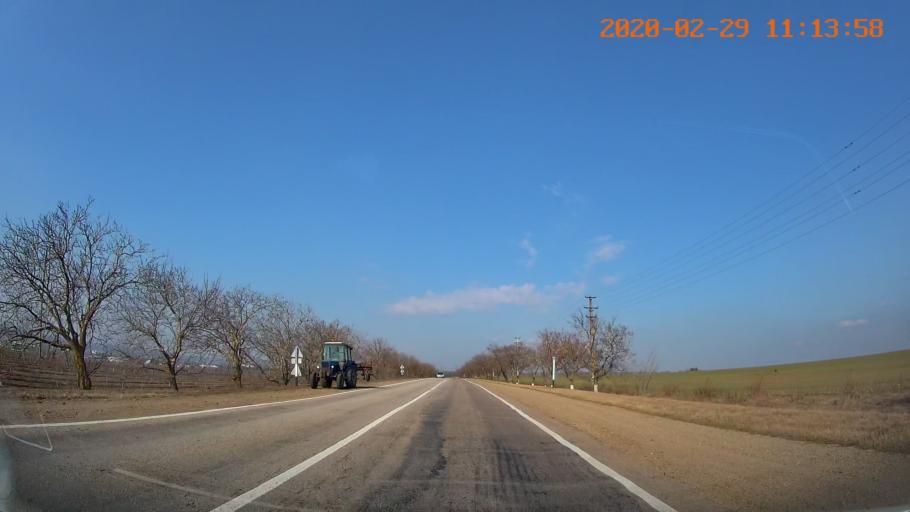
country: MD
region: Telenesti
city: Dubasari
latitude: 47.2775
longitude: 29.1777
